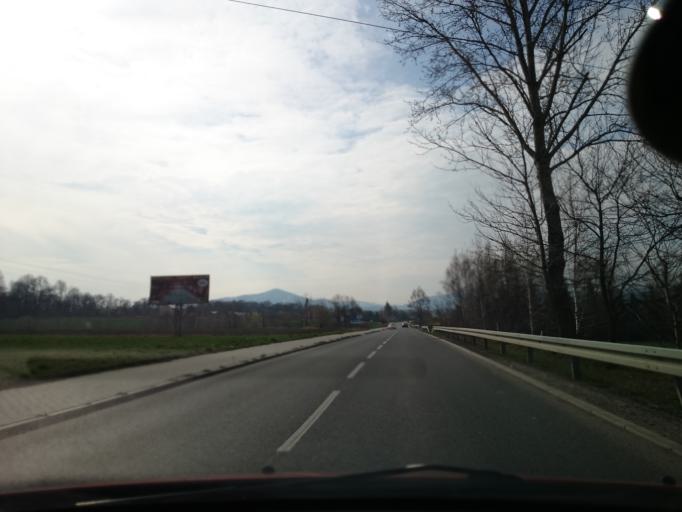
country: PL
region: Opole Voivodeship
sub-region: Powiat nyski
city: Glucholazy
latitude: 50.3330
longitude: 17.3899
